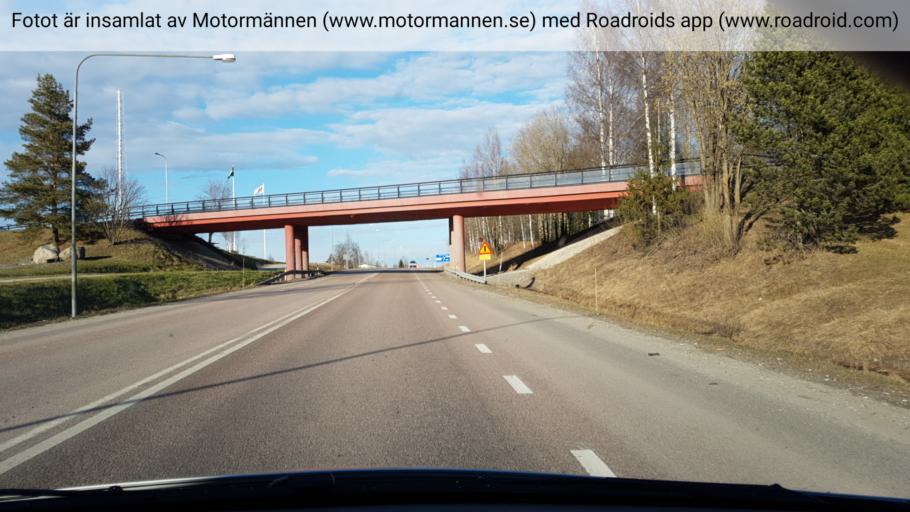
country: SE
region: Vaesternorrland
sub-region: OErnskoeldsviks Kommun
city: Ornskoldsvik
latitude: 63.3019
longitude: 18.7230
